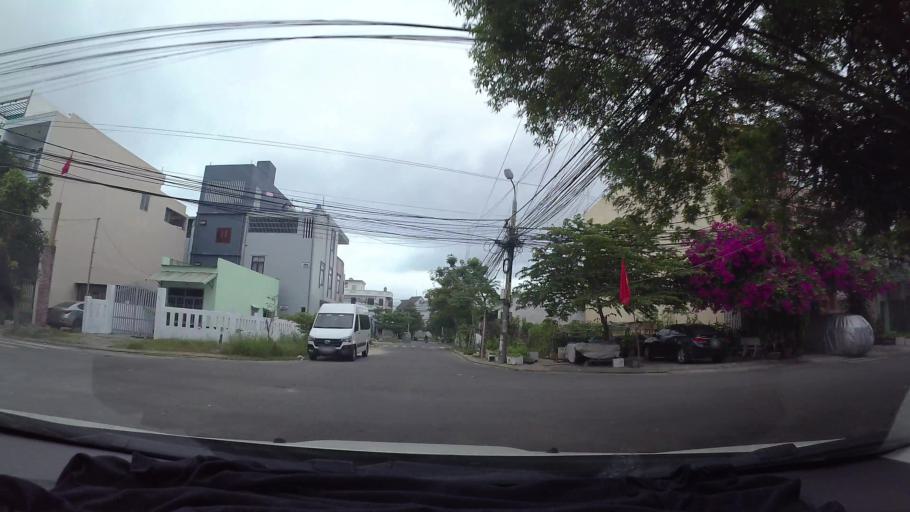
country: VN
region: Da Nang
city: Da Nang
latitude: 16.0856
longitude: 108.2336
